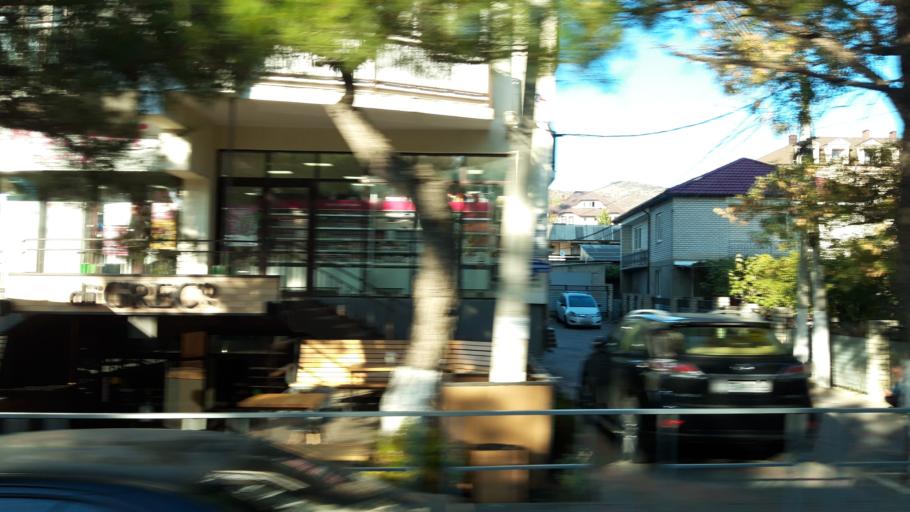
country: RU
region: Krasnodarskiy
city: Kabardinka
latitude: 44.6512
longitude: 37.9401
